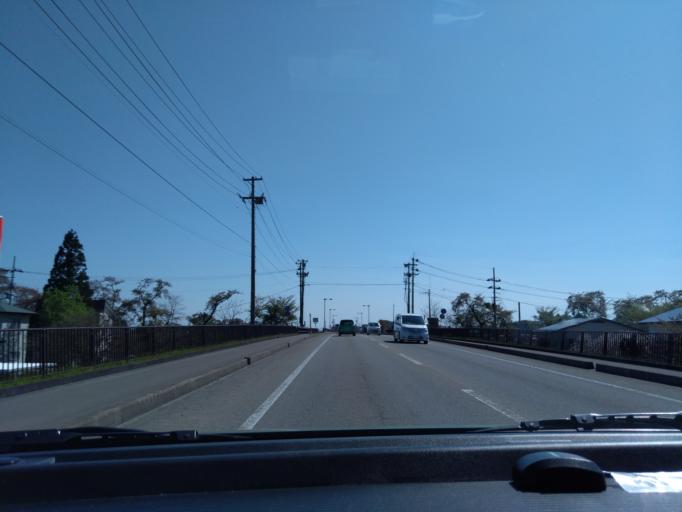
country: JP
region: Akita
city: Kakunodatemachi
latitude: 39.5818
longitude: 140.5688
